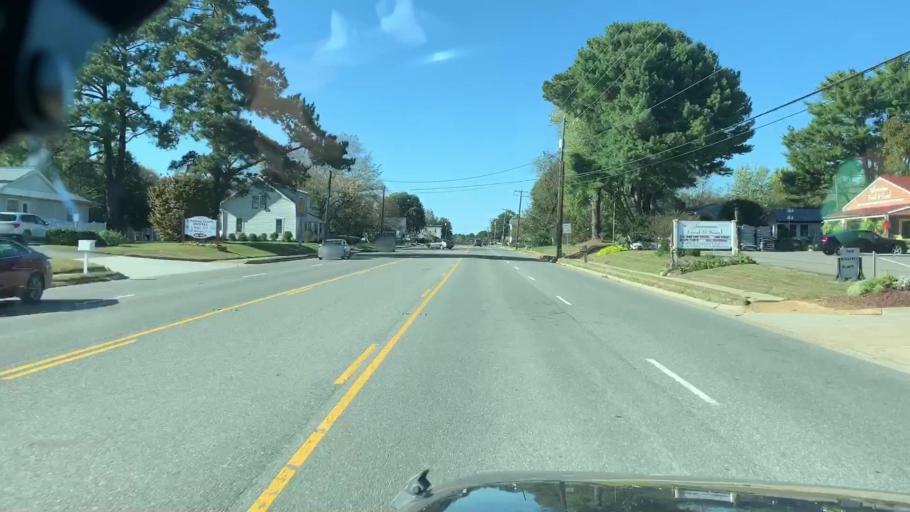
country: US
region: Virginia
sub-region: James City County
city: Williamsburg
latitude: 37.3657
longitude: -76.7681
